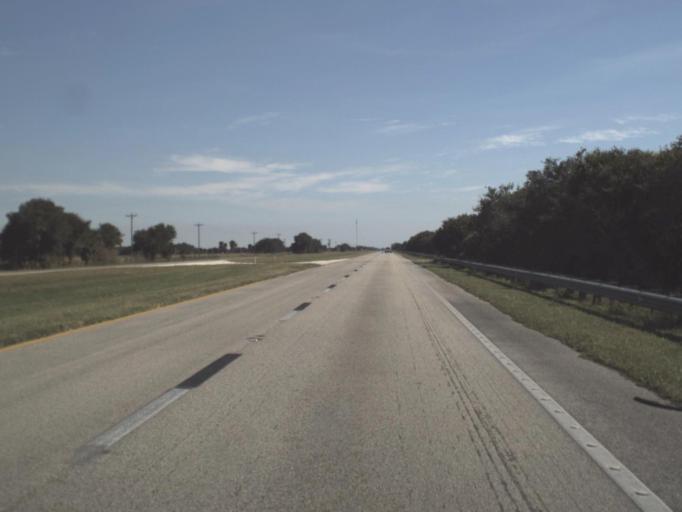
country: US
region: Florida
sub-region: Glades County
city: Moore Haven
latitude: 26.8894
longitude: -81.2345
